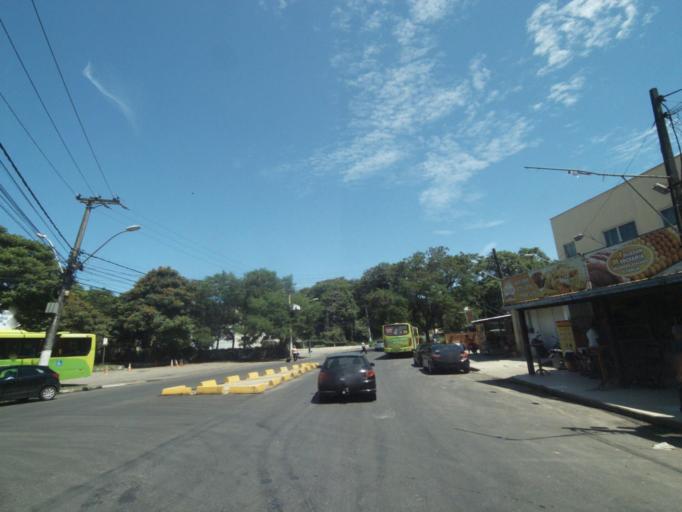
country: BR
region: Rio de Janeiro
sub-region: Sao Goncalo
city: Sao Goncalo
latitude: -22.9104
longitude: -42.9858
